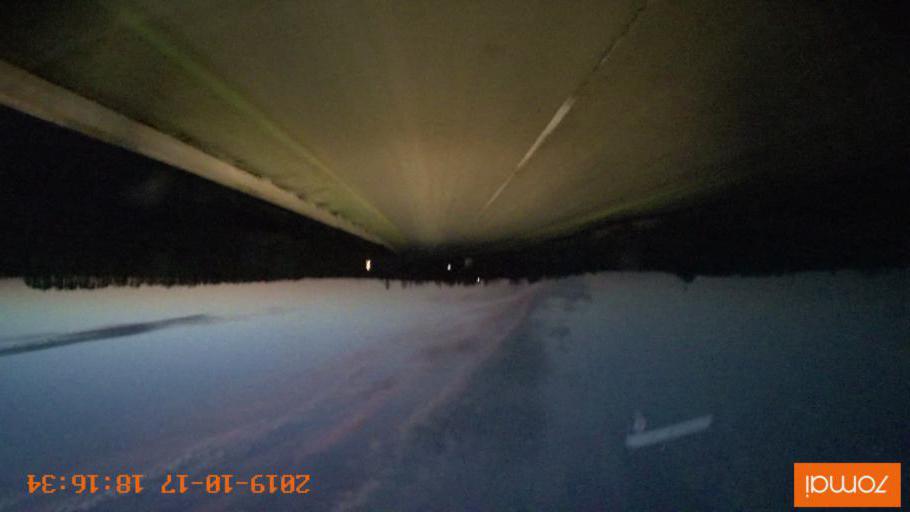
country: RU
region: Tula
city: Kurkino
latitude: 53.3980
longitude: 38.5153
